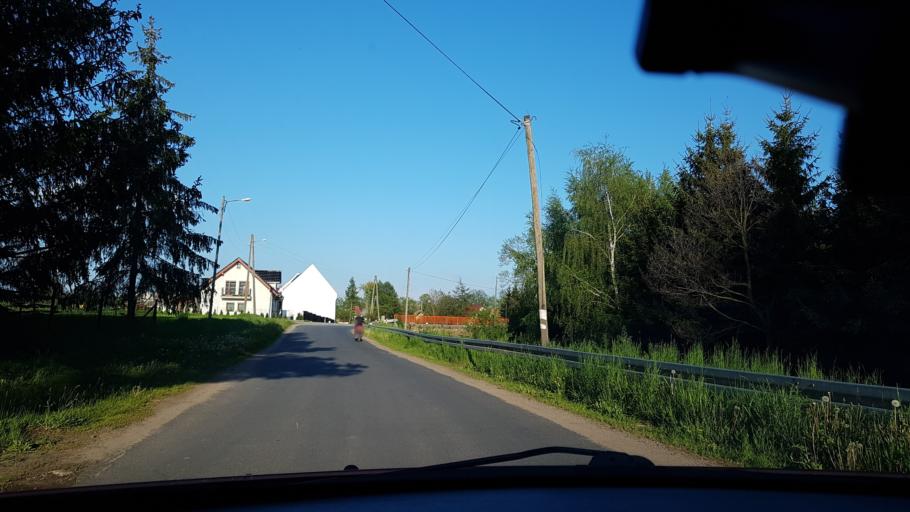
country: PL
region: Lower Silesian Voivodeship
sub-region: Powiat zabkowicki
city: Budzow
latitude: 50.6099
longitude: 16.7077
